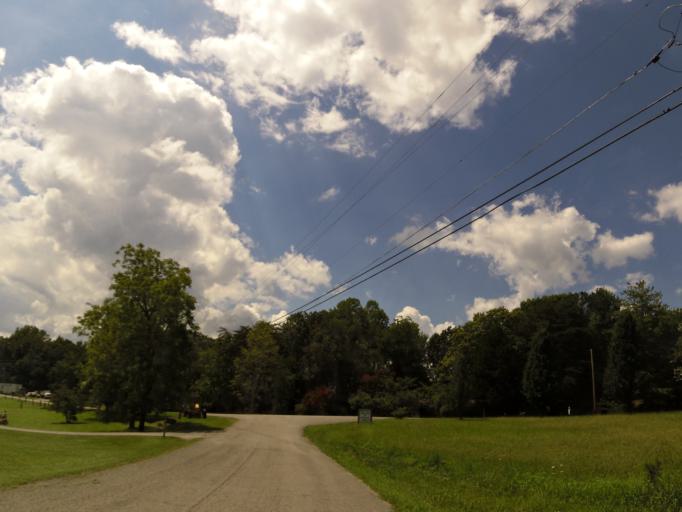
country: US
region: Tennessee
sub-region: Roane County
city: Rockwood
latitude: 35.8969
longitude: -84.7660
